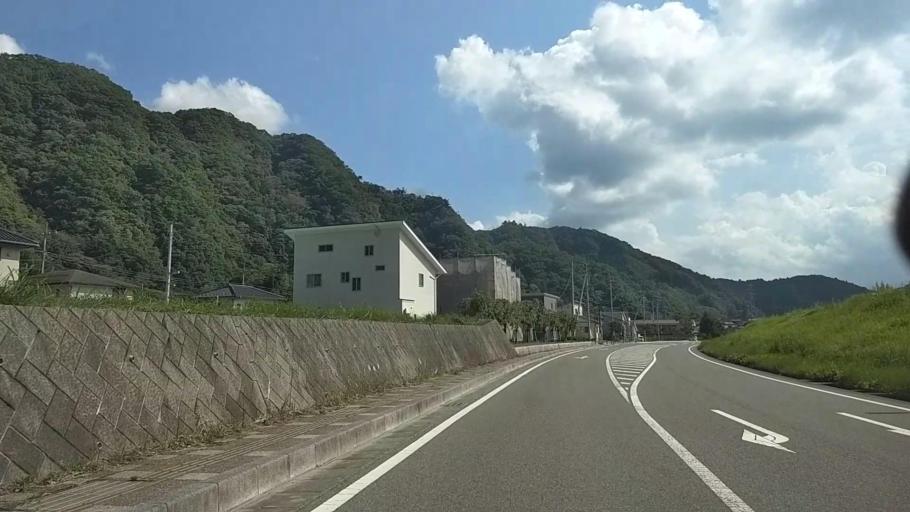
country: JP
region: Shizuoka
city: Fujinomiya
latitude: 35.3700
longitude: 138.4540
